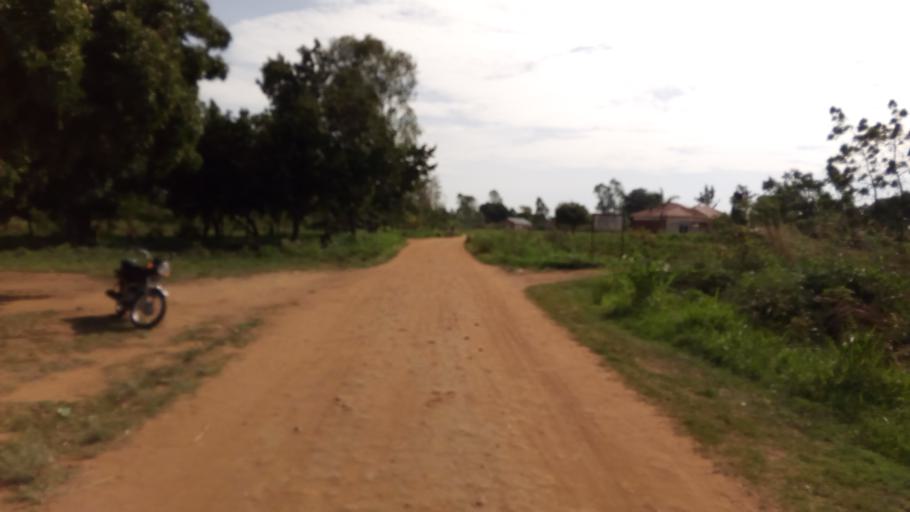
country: UG
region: Northern Region
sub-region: Gulu District
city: Gulu
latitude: 2.7946
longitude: 32.3262
